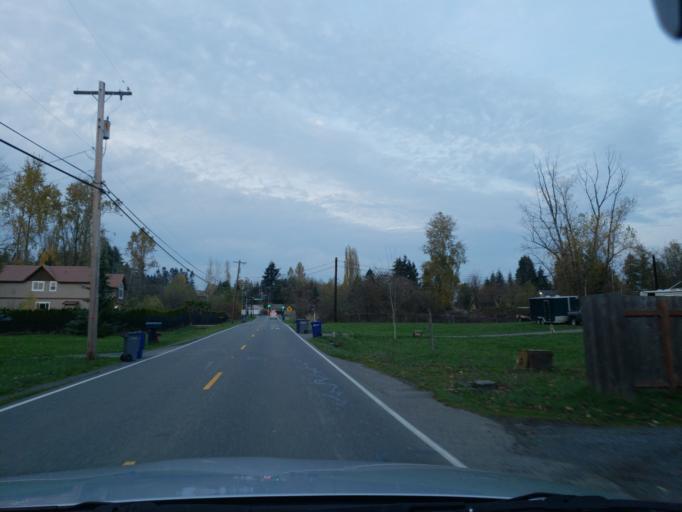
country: US
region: Washington
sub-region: King County
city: Bothell
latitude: 47.7784
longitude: -122.2232
